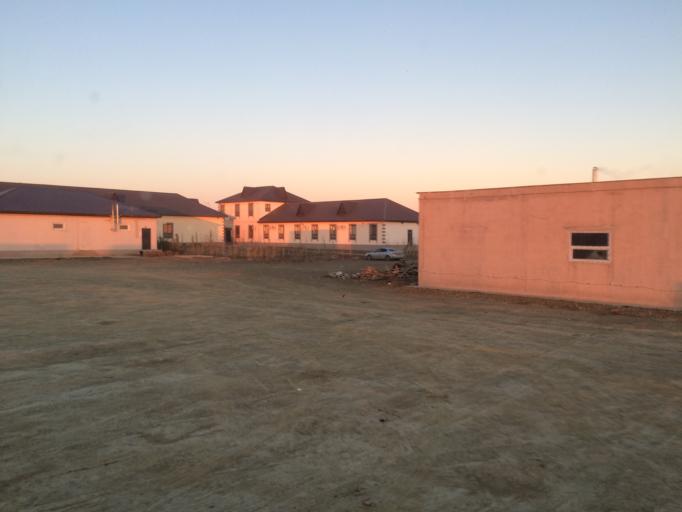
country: RU
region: Orenburg
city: Dombarovskiy
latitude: 49.9689
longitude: 60.0628
